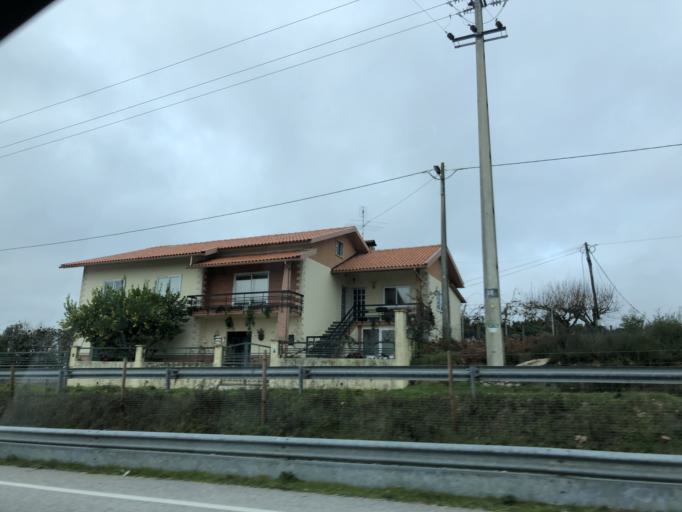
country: PT
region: Viseu
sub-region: Santa Comba Dao
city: Santa Comba Dao
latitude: 40.3551
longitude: -8.1506
